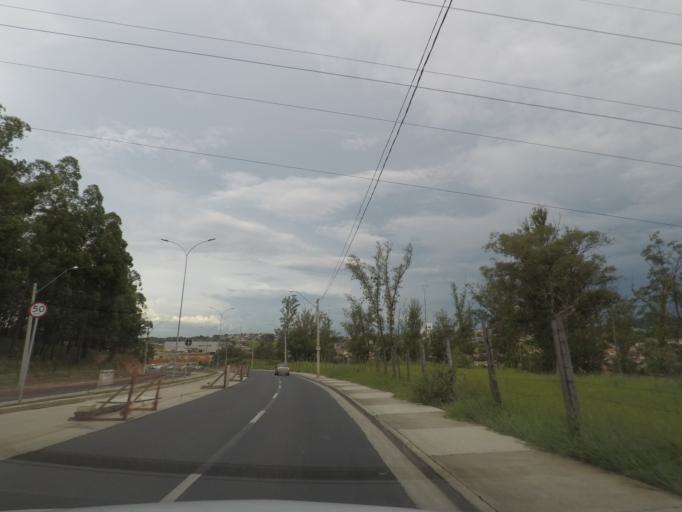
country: BR
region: Sao Paulo
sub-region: Hortolandia
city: Hortolandia
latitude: -22.9384
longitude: -47.1660
